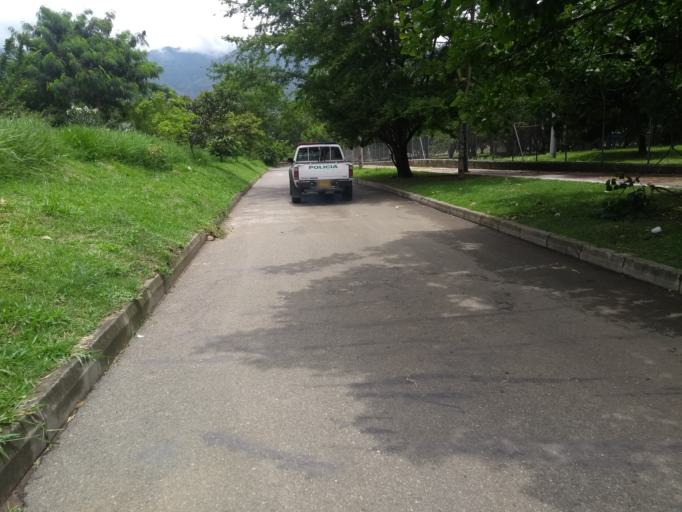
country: CO
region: Antioquia
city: Bello
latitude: 6.3326
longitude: -75.5487
